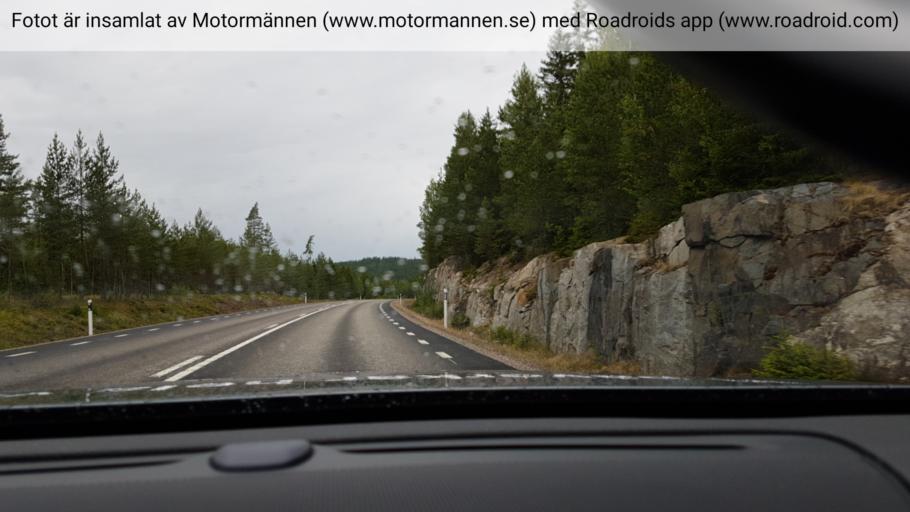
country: SE
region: Dalarna
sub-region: Faluns Kommun
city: Bjursas
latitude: 60.7875
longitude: 15.2851
